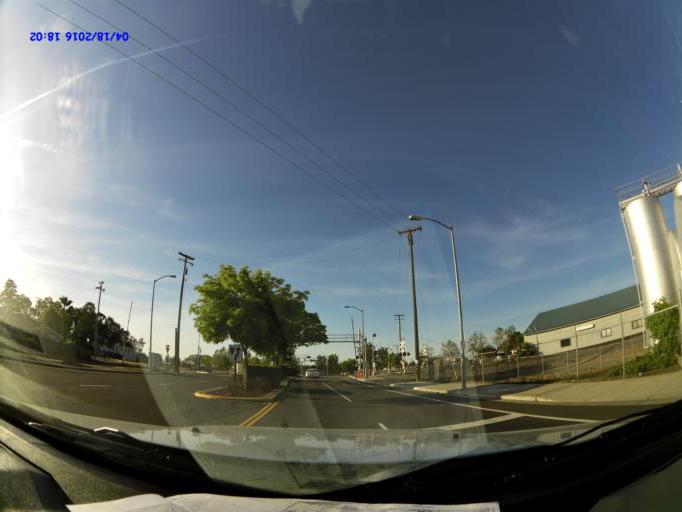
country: US
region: California
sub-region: San Joaquin County
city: Escalon
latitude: 37.7961
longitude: -120.9966
